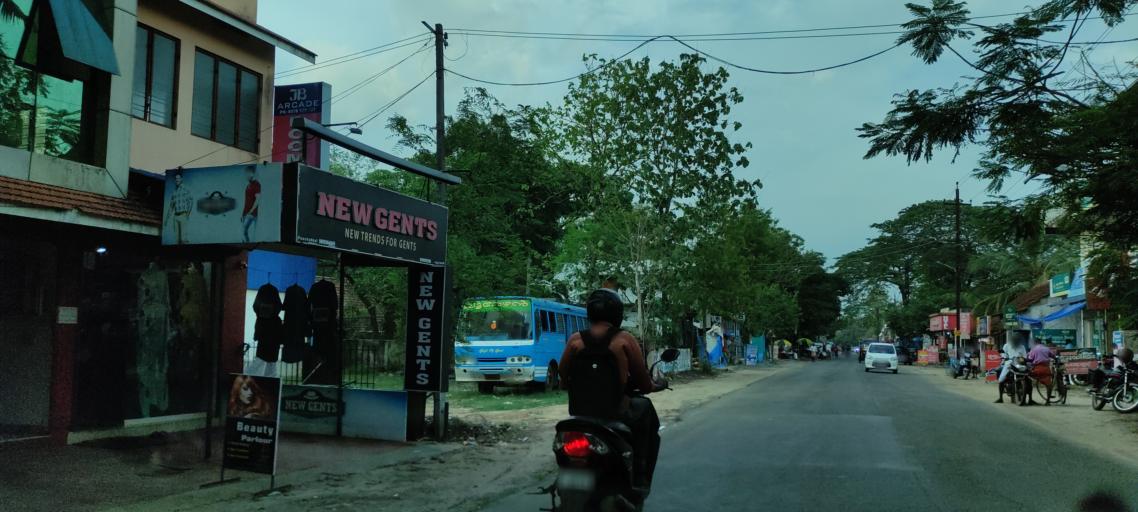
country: IN
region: Kerala
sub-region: Alappuzha
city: Kutiatodu
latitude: 9.8019
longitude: 76.3536
